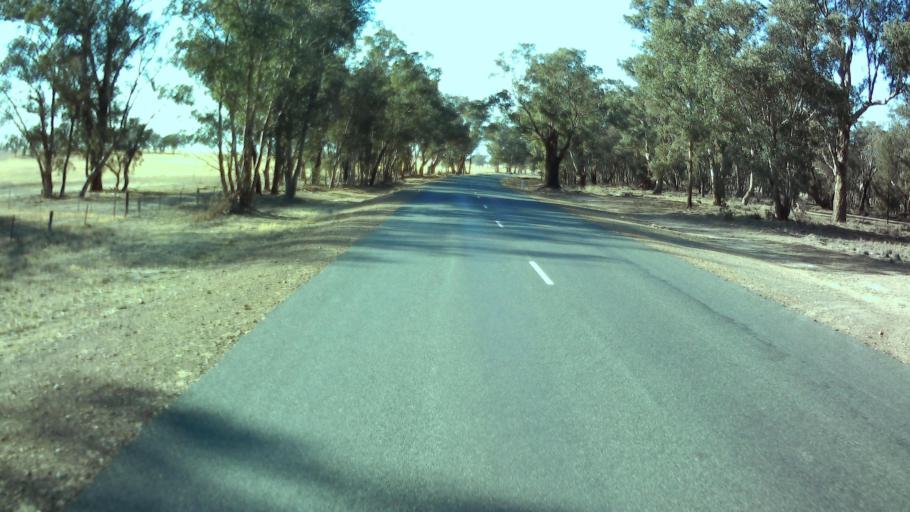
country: AU
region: New South Wales
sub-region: Weddin
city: Grenfell
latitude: -33.9499
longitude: 148.1379
